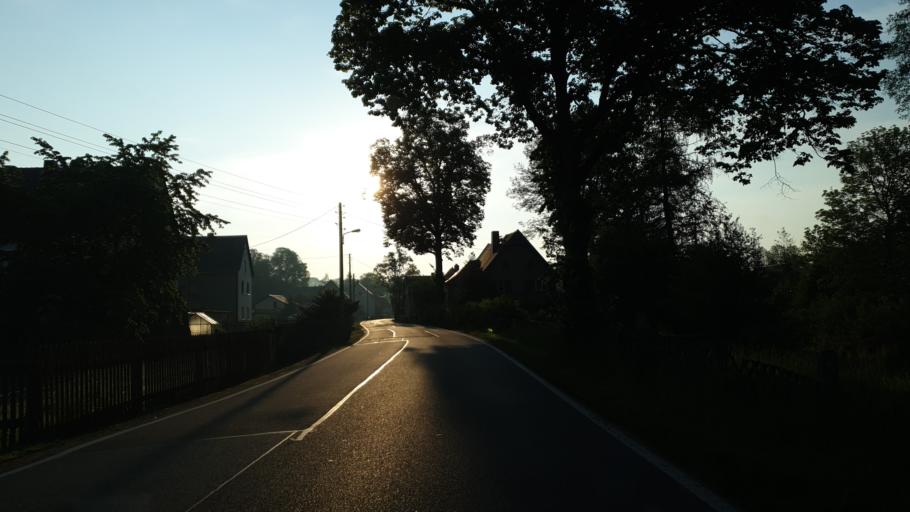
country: DE
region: Saxony
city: Sankt Egidien
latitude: 50.7840
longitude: 12.6283
